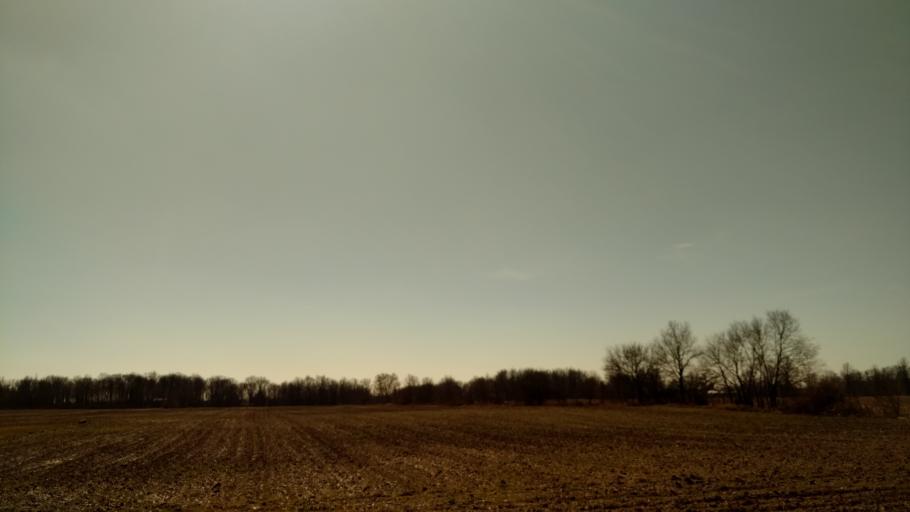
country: US
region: Ohio
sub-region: Marion County
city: Prospect
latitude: 40.4982
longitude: -83.1261
